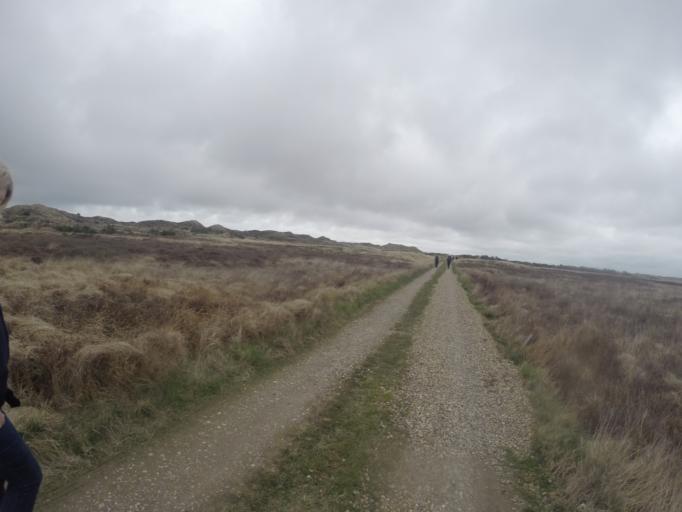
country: DK
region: North Denmark
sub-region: Thisted Kommune
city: Hurup
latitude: 56.8877
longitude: 8.3224
